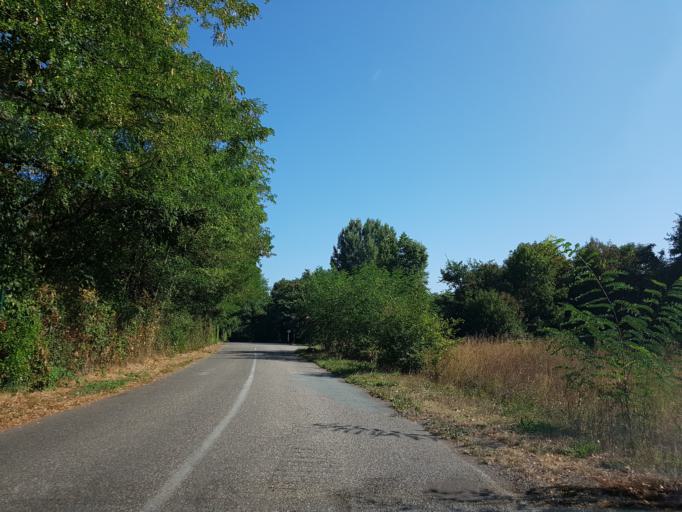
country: FR
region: Alsace
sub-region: Departement du Haut-Rhin
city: Pulversheim
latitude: 47.8452
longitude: 7.2852
